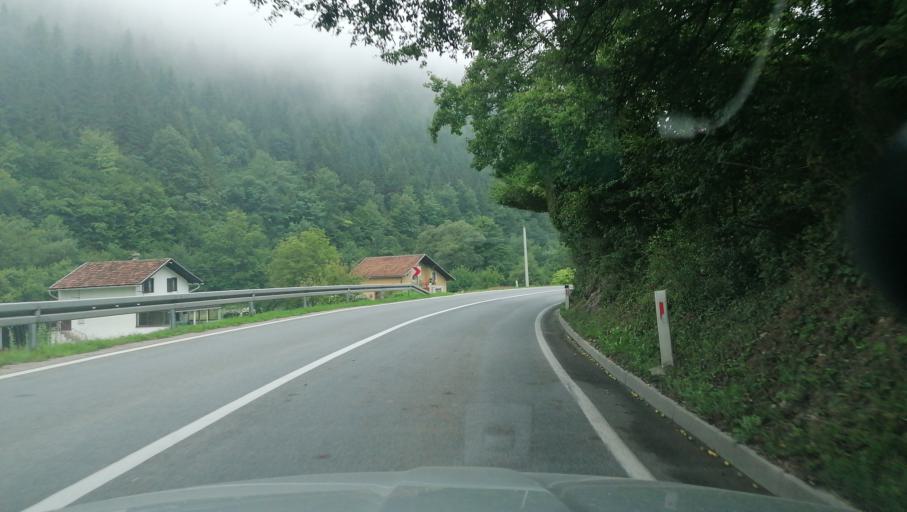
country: BA
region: Federation of Bosnia and Herzegovina
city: Donji Vakuf
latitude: 44.1534
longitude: 17.3708
